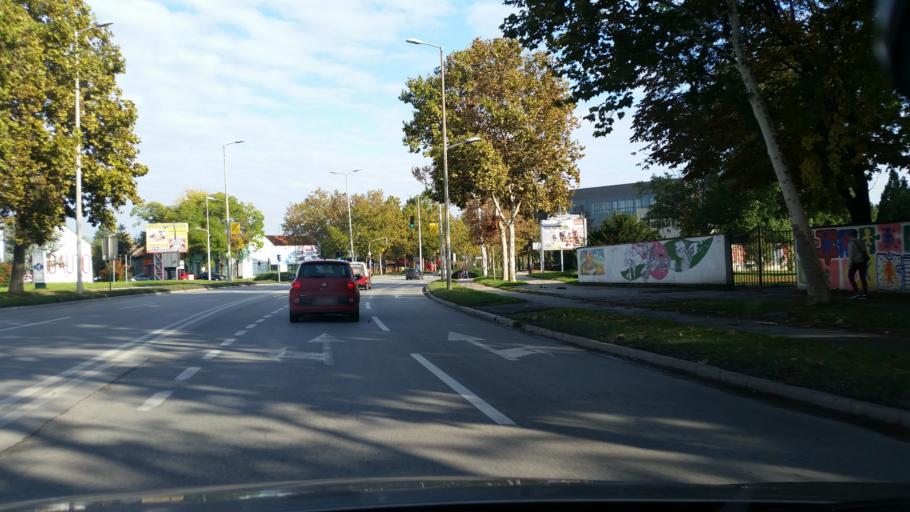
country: RS
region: Autonomna Pokrajina Vojvodina
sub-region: Srednjebanatski Okrug
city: Zrenjanin
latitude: 45.3835
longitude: 20.3924
